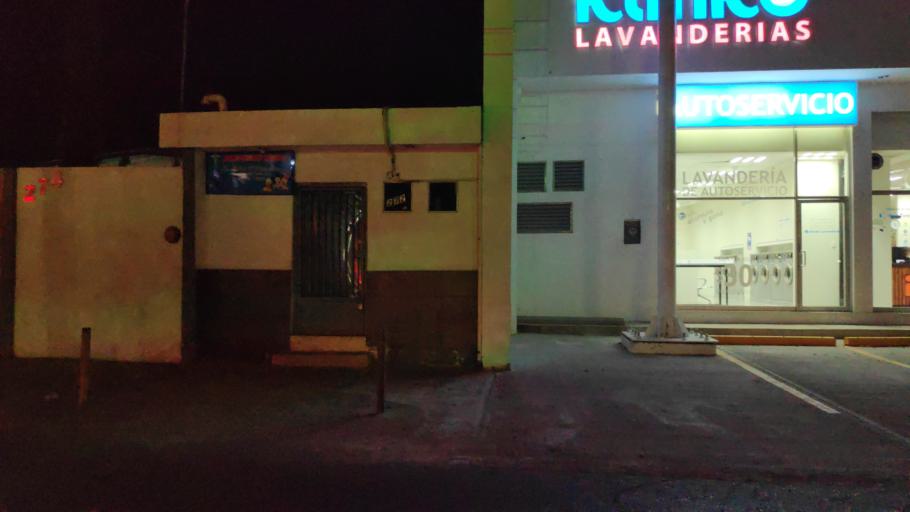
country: MX
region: Sinaloa
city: Culiacan
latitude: 24.8315
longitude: -107.3901
